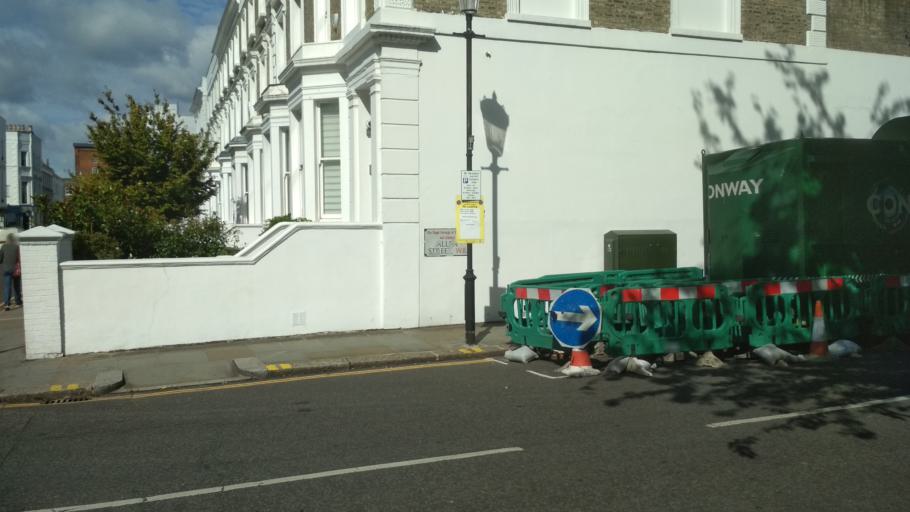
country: GB
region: England
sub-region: Greater London
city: Kensington
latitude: 51.4981
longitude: -0.1947
